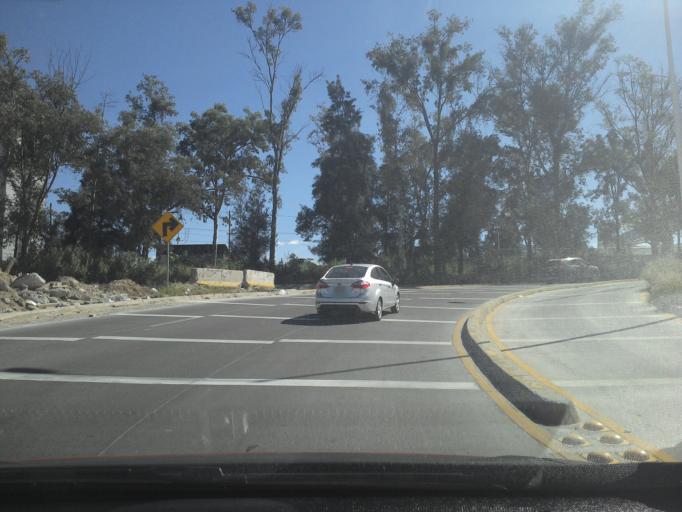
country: MX
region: Jalisco
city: Zapopan2
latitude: 20.7194
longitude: -103.4261
